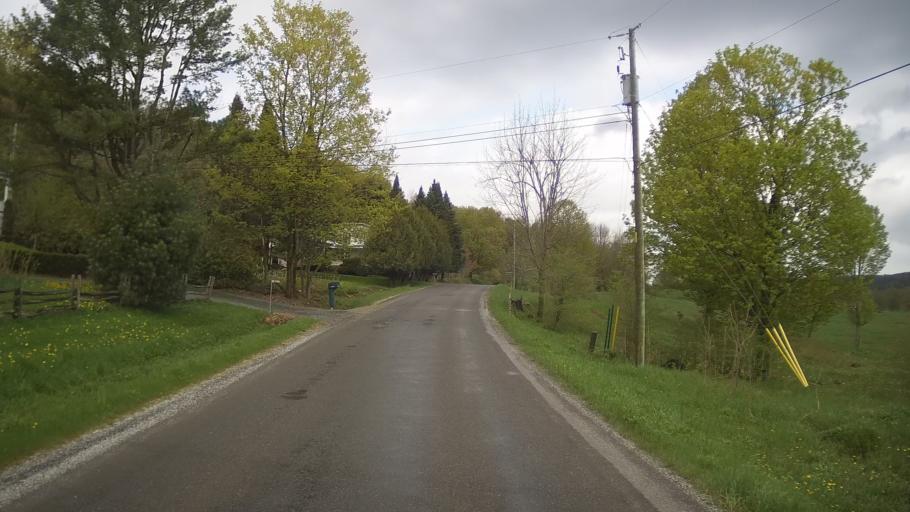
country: CA
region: Quebec
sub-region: Monteregie
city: Cowansville
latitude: 45.1914
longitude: -72.7010
